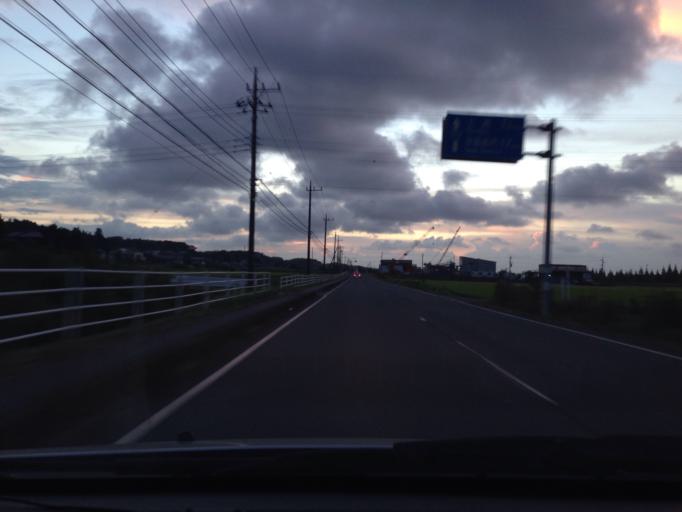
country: JP
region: Ibaraki
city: Ami
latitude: 36.0334
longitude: 140.2530
